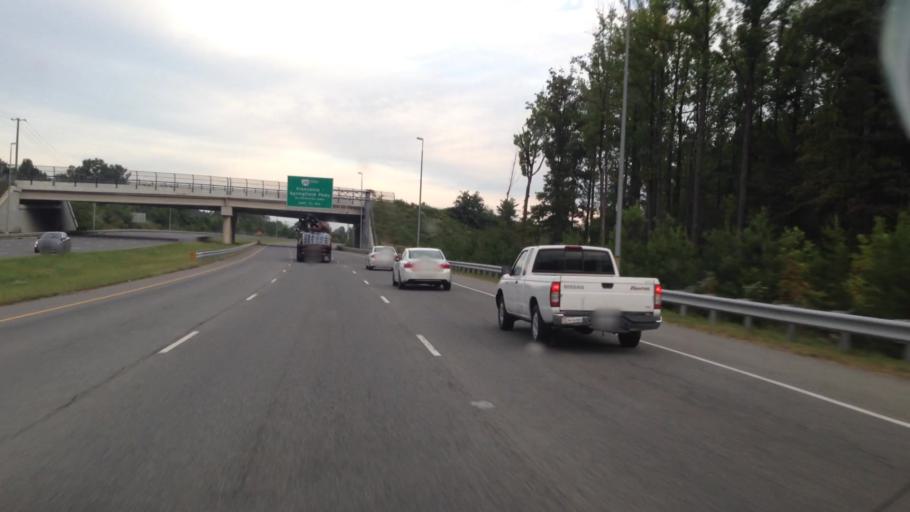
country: US
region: Virginia
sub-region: Fairfax County
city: West Springfield
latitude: 38.7514
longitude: -77.2131
